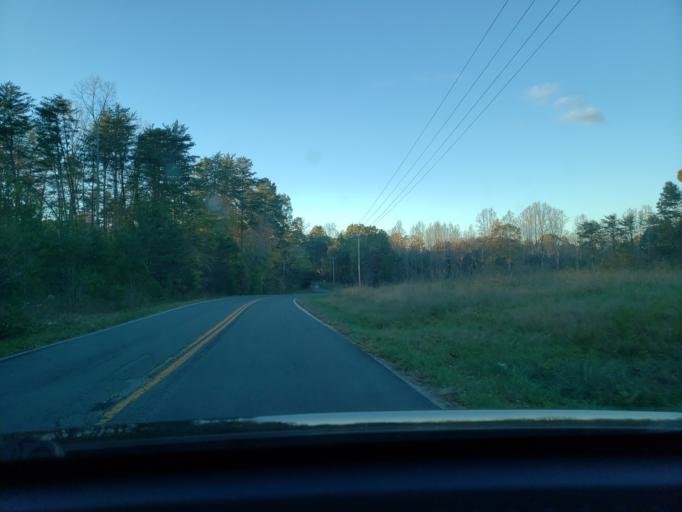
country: US
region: North Carolina
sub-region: Stokes County
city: Danbury
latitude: 36.3773
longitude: -80.1882
